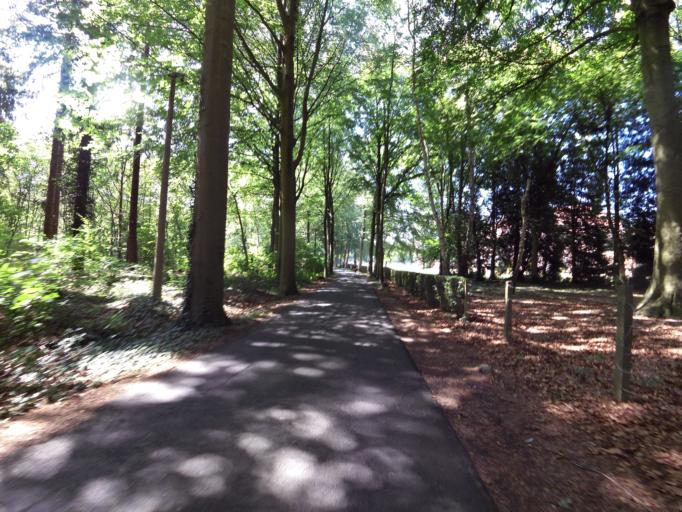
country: BE
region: Flanders
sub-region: Provincie West-Vlaanderen
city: Zedelgem
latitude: 51.1577
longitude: 3.1640
